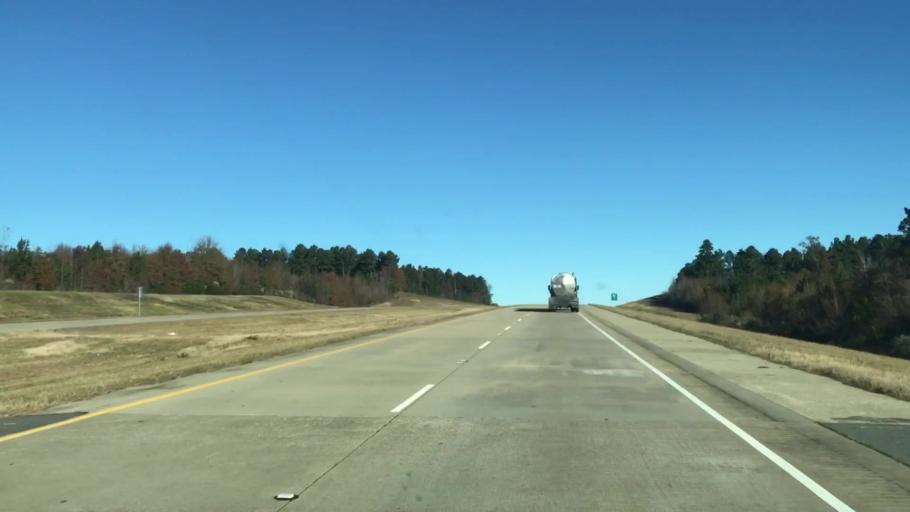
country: US
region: Louisiana
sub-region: Caddo Parish
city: Vivian
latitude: 32.9870
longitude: -93.9105
